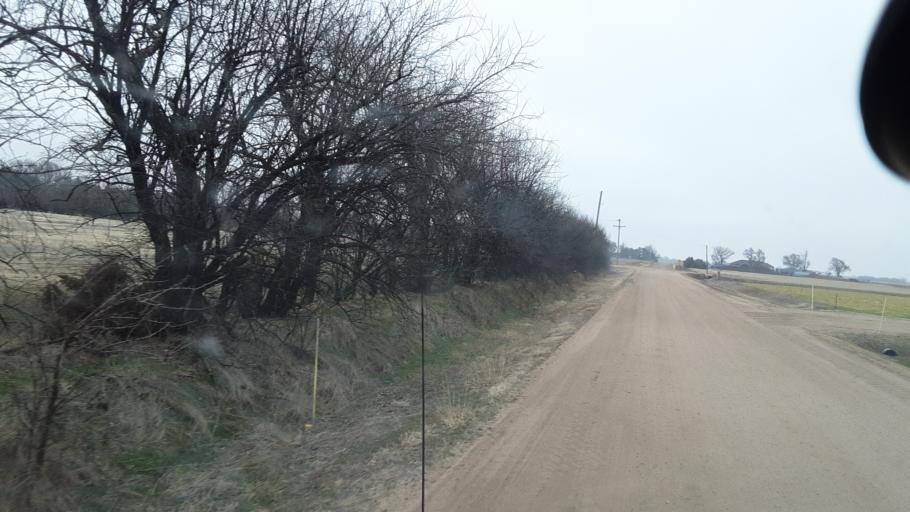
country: US
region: Kansas
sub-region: Reno County
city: South Hutchinson
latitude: 37.9845
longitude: -97.9974
